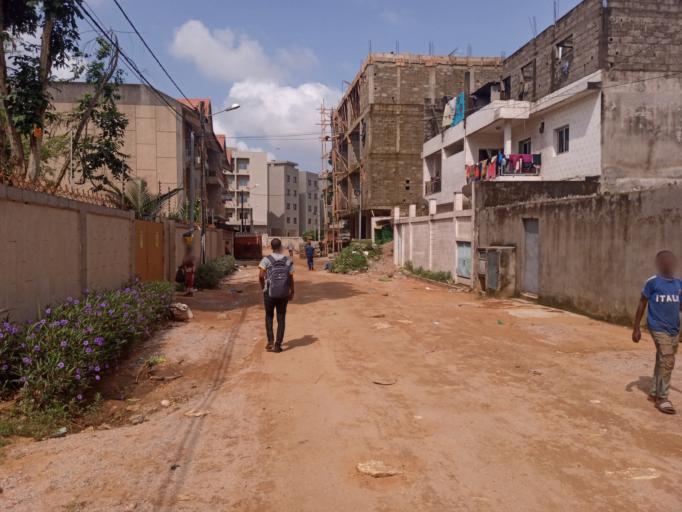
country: CI
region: Lagunes
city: Bingerville
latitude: 5.3640
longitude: -3.9573
